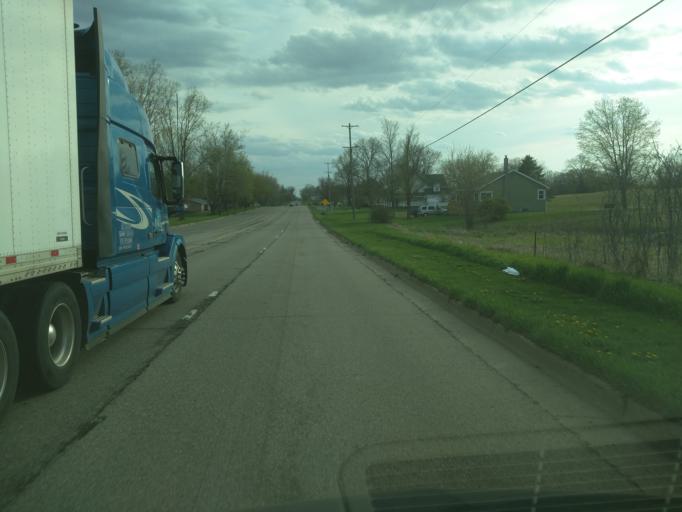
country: US
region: Michigan
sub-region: Eaton County
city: Eaton Rapids
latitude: 42.5286
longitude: -84.6418
